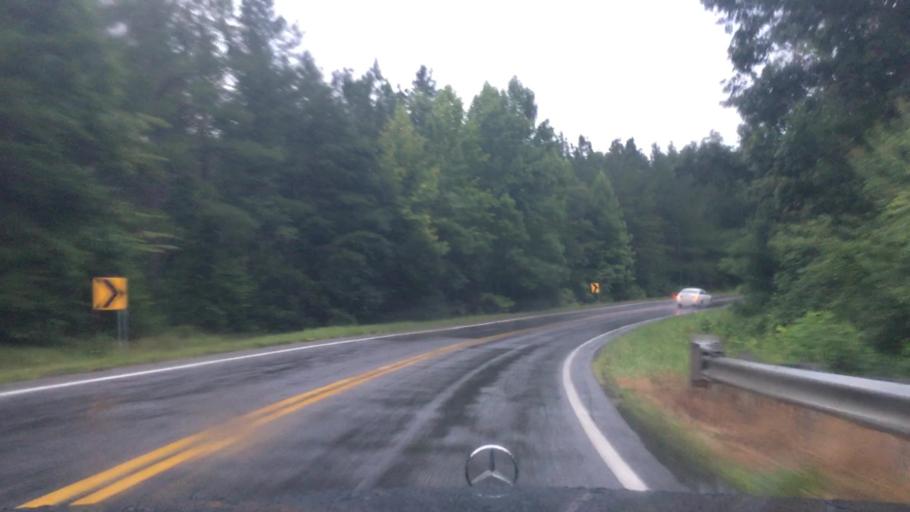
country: US
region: Virginia
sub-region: Campbell County
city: Timberlake
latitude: 37.2411
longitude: -79.2801
